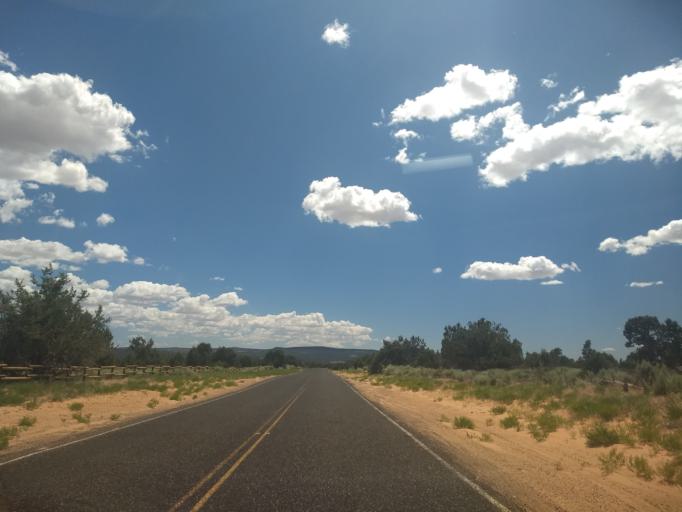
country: US
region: Utah
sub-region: Kane County
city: Kanab
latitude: 37.0405
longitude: -112.7290
